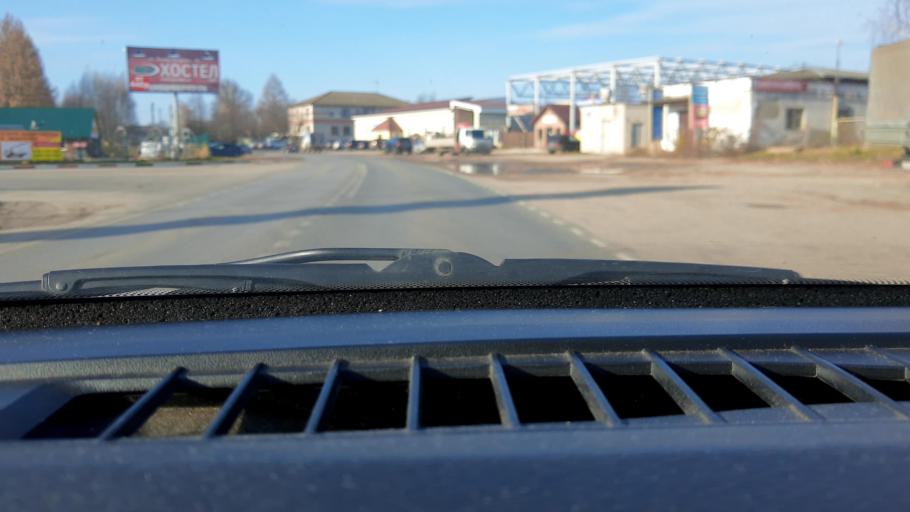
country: RU
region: Nizjnij Novgorod
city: Gorodets
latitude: 56.6408
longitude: 43.5002
